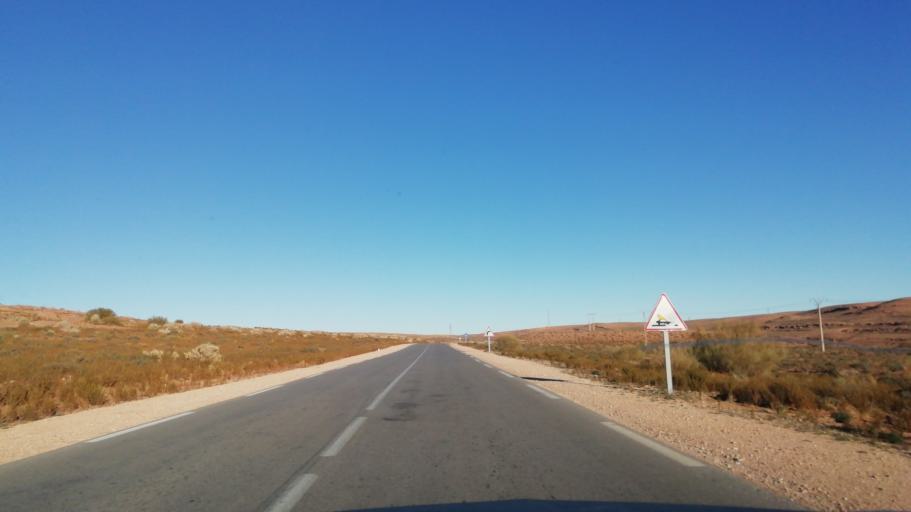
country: DZ
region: El Bayadh
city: El Abiodh Sidi Cheikh
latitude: 33.1677
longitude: 0.4229
